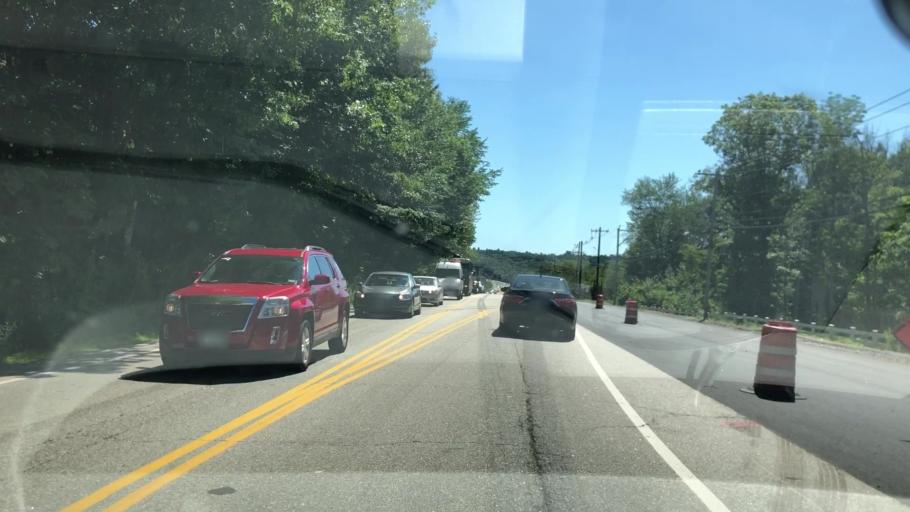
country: US
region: New Hampshire
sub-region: Hillsborough County
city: Bedford
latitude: 42.9439
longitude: -71.5161
